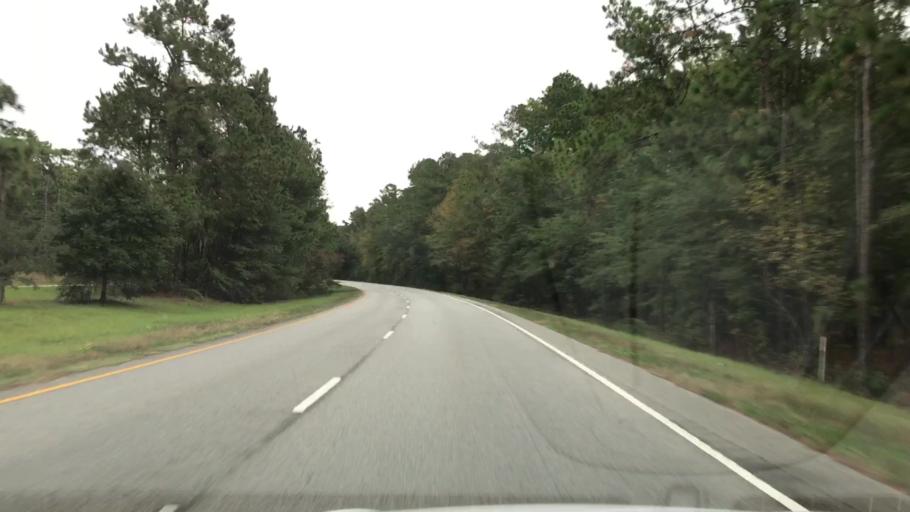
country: US
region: South Carolina
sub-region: Georgetown County
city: Georgetown
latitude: 33.3649
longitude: -79.2249
